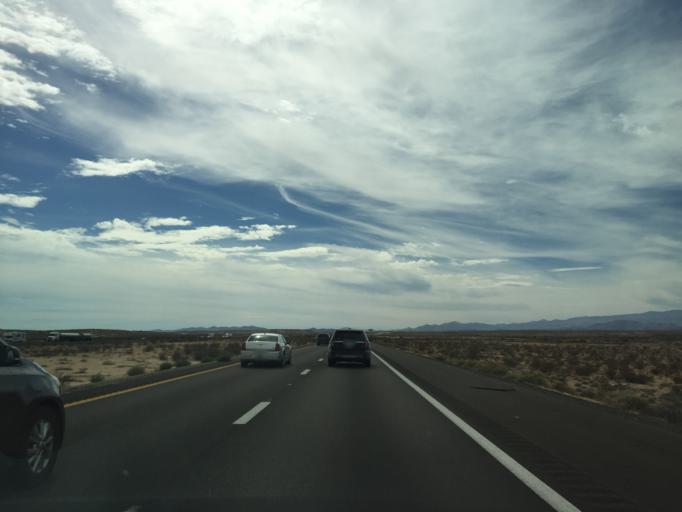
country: US
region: Nevada
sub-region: Clark County
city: Moapa Town
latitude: 36.5647
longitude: -114.6799
